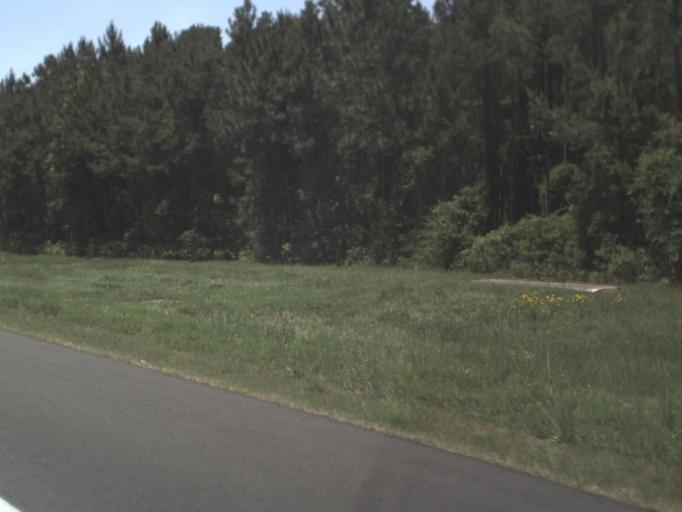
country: US
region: Florida
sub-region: Nassau County
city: Yulee
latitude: 30.6528
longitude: -81.6619
